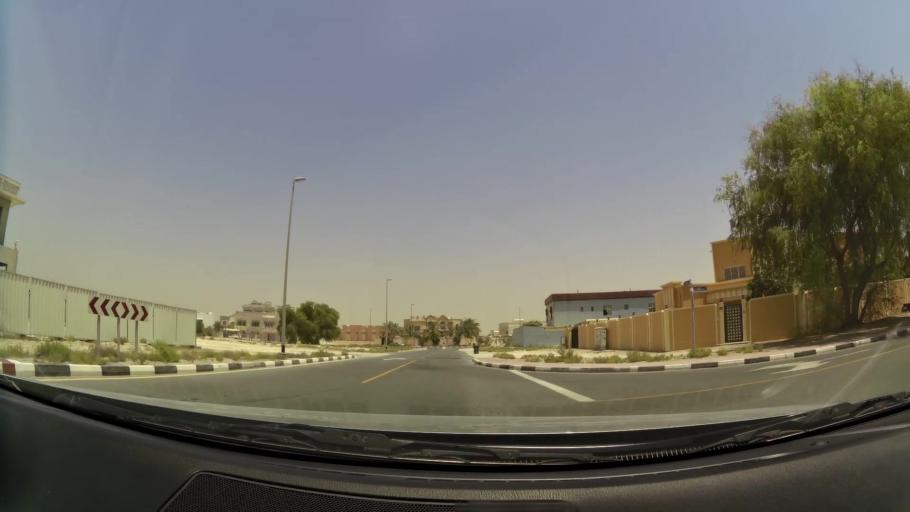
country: AE
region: Dubai
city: Dubai
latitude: 25.0915
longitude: 55.1962
